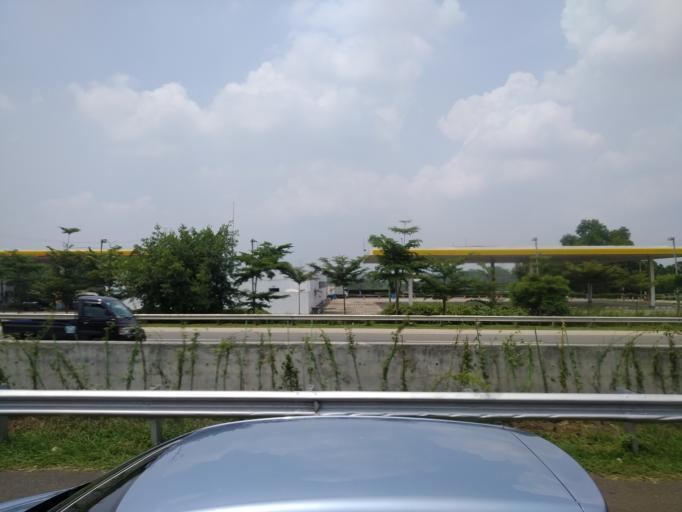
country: ID
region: West Java
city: Citeureup
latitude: -6.4349
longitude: 106.8941
